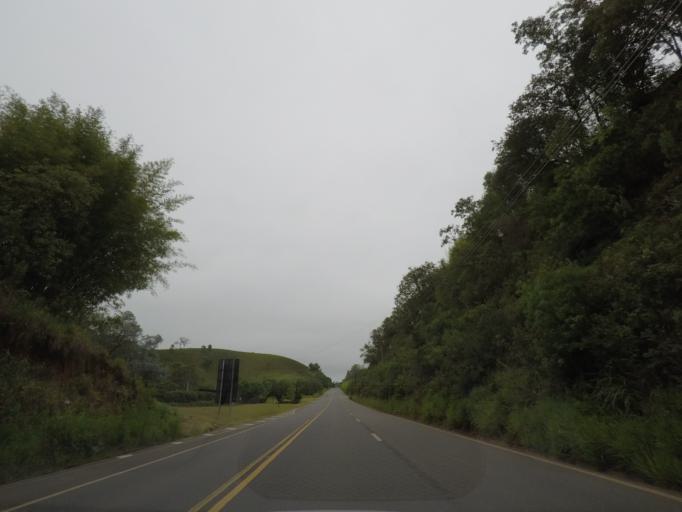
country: BR
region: Sao Paulo
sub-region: Cunha
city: Cunha
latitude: -23.0574
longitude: -44.9872
